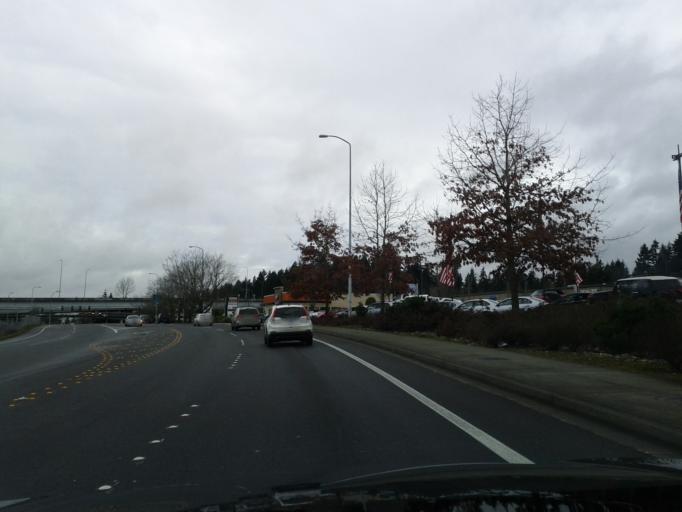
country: US
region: Washington
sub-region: King County
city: Eastgate
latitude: 47.5806
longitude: -122.1379
